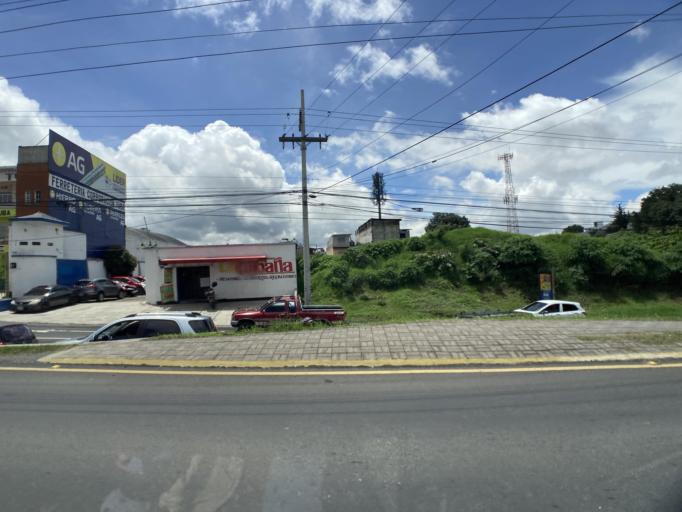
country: GT
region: Guatemala
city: Mixco
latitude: 14.6131
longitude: -90.6014
